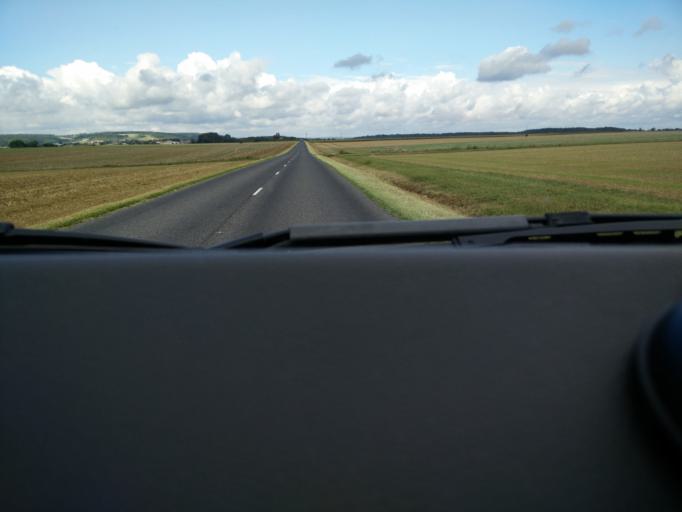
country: FR
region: Lorraine
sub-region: Departement de la Meuse
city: Etain
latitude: 49.1020
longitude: 5.6203
